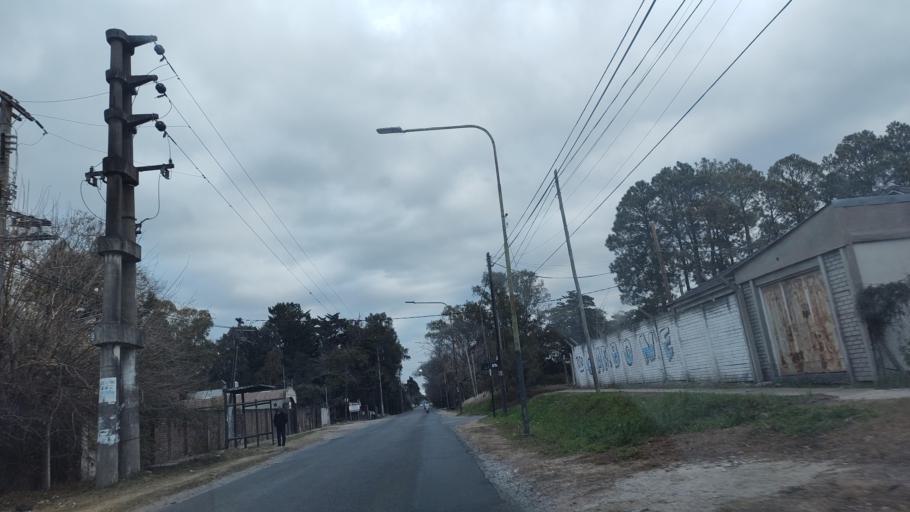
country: AR
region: Buenos Aires
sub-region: Partido de La Plata
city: La Plata
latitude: -34.8642
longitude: -58.0916
